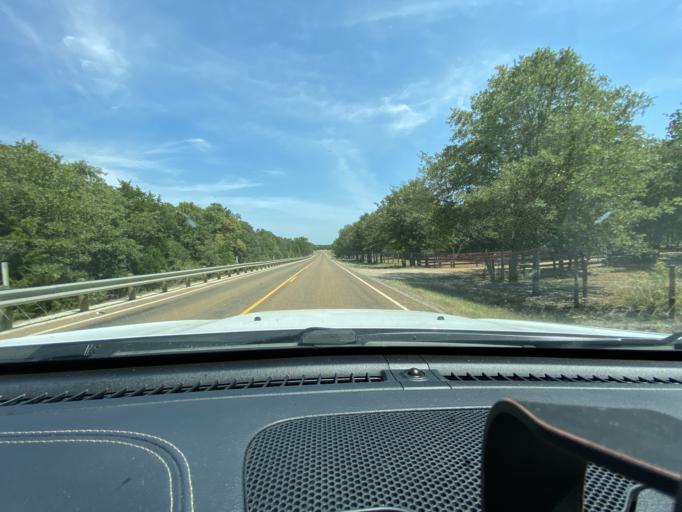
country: US
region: Texas
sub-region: Bastrop County
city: Smithville
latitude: 30.1341
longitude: -97.0803
